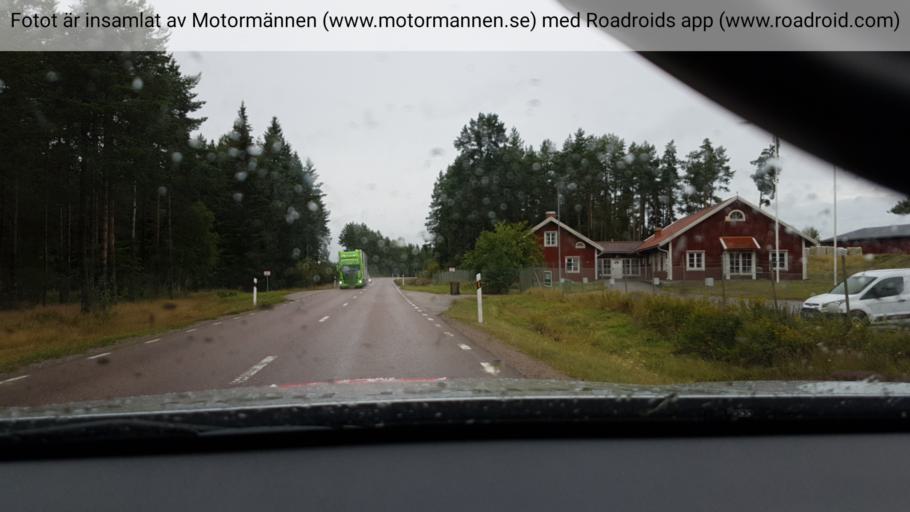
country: SE
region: Gaevleborg
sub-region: Gavle Kommun
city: Valbo
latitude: 60.5361
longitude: 16.9445
